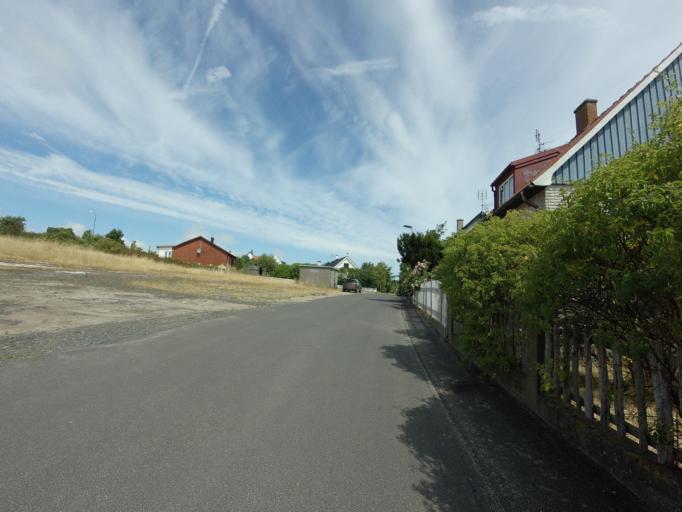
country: SE
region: Skane
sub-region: Simrishamns Kommun
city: Simrishamn
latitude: 55.5433
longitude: 14.3570
